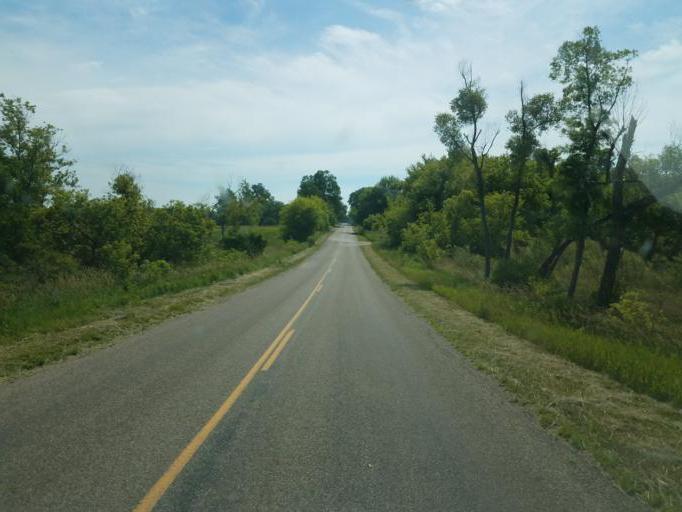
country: US
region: Michigan
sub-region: Barry County
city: Nashville
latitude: 42.6833
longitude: -85.0084
